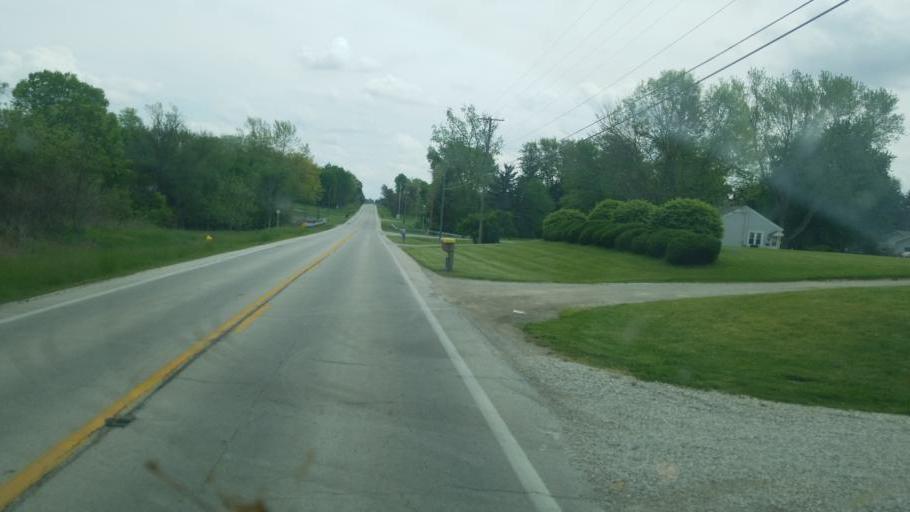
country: US
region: Ohio
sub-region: Seneca County
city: Tiffin
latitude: 41.0940
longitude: -83.1625
